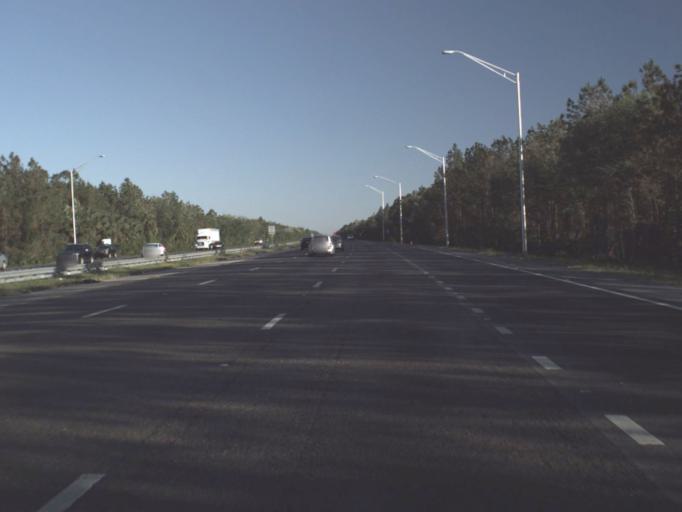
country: US
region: Florida
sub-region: Flagler County
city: Palm Coast
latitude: 29.5945
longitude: -81.2454
